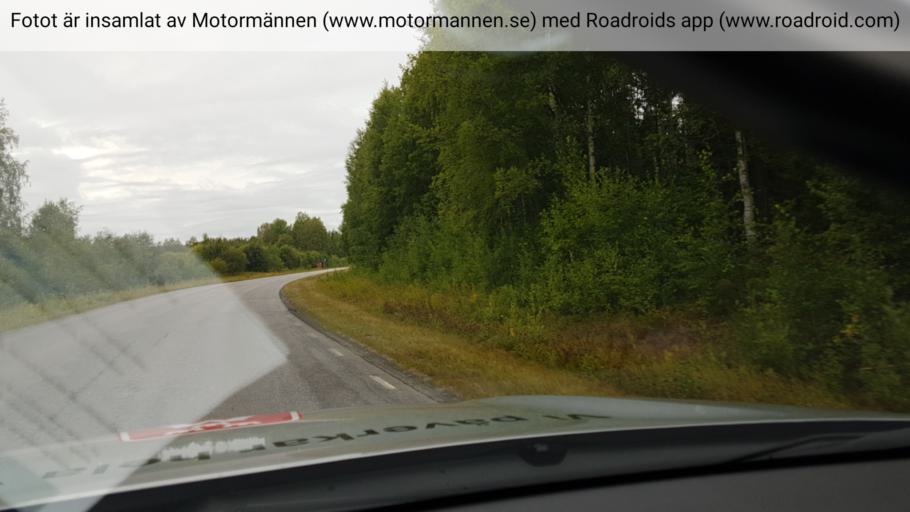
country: SE
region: Norrbotten
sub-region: Bodens Kommun
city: Boden
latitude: 65.8142
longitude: 21.6273
